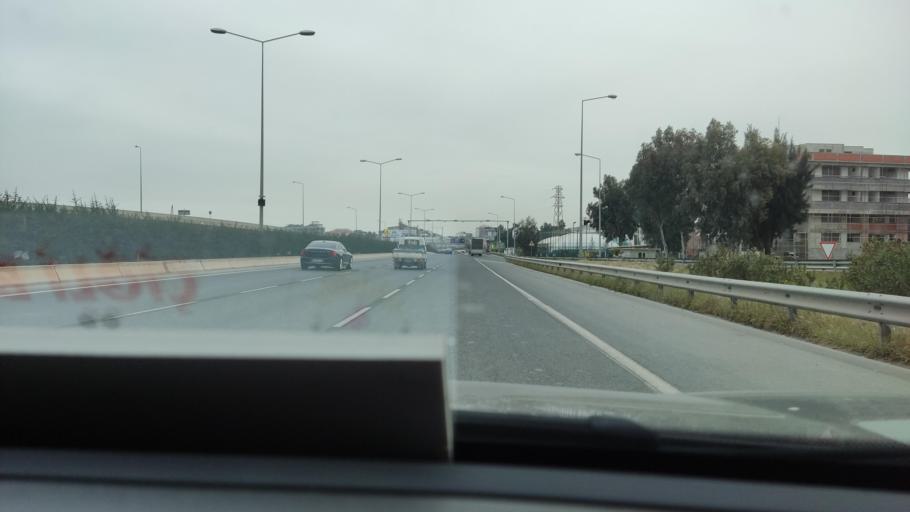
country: TR
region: Izmir
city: Karsiyaka
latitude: 38.4868
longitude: 27.0800
